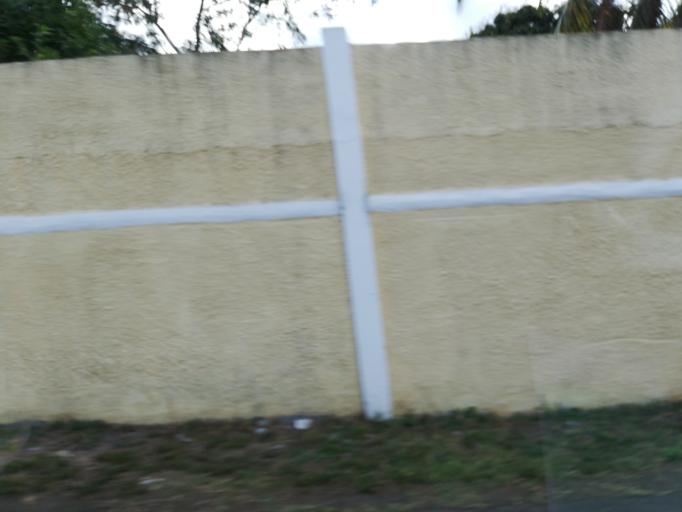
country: MU
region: Plaines Wilhems
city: Ebene
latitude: -20.2356
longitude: 57.4621
